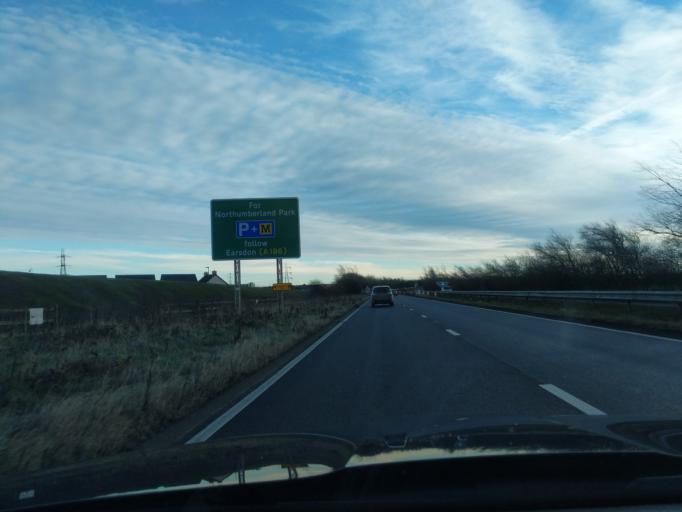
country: GB
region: England
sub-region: Northumberland
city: Backworth
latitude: 55.0354
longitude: -1.5337
